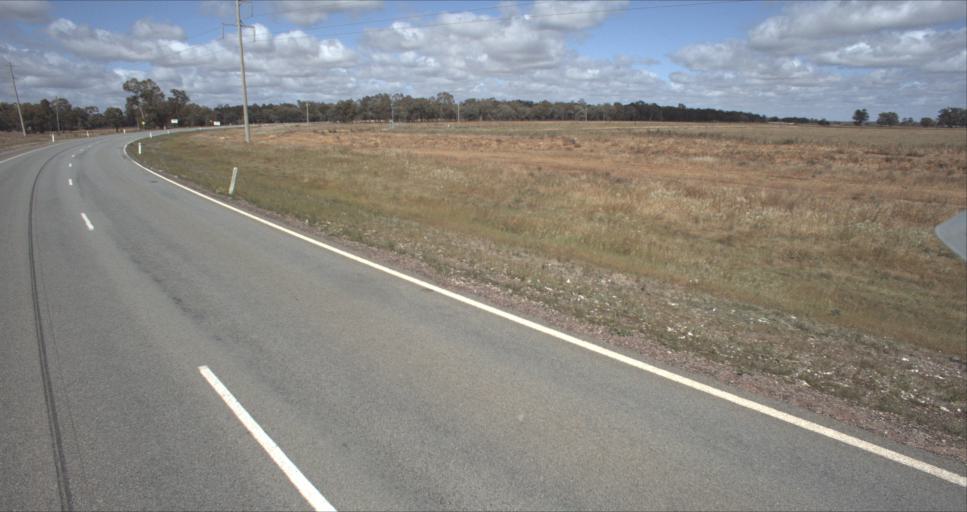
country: AU
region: New South Wales
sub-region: Murrumbidgee Shire
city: Darlington Point
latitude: -34.5953
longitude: 146.1628
